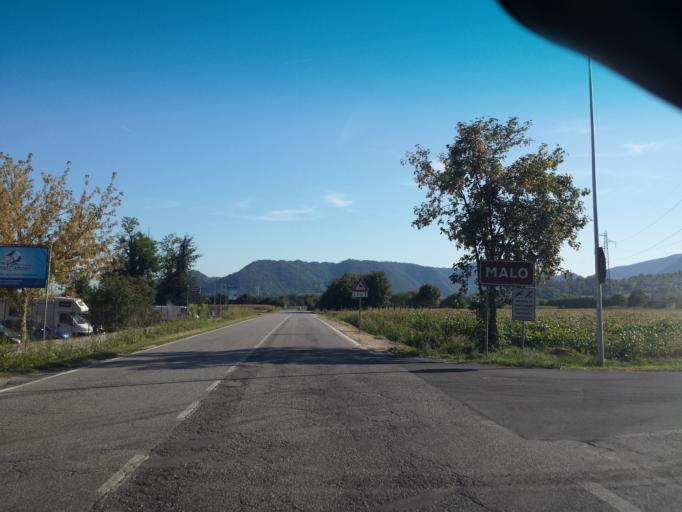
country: IT
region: Veneto
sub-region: Provincia di Vicenza
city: San Vito di Leguzzano
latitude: 45.6795
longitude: 11.3851
